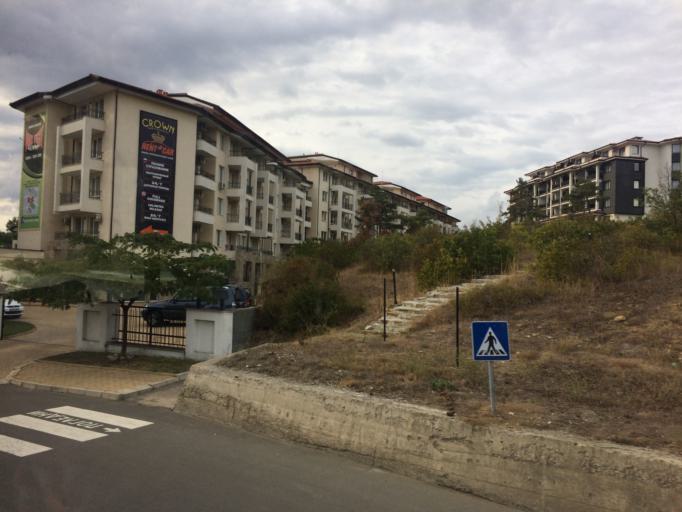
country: BG
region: Burgas
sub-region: Obshtina Nesebur
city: Sveti Vlas
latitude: 42.7104
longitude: 27.7258
